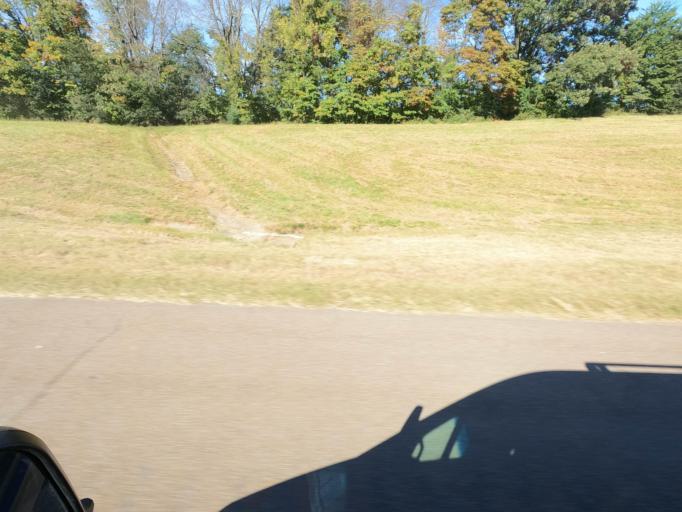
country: US
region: Tennessee
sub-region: Obion County
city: South Fulton
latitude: 36.4951
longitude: -88.9091
